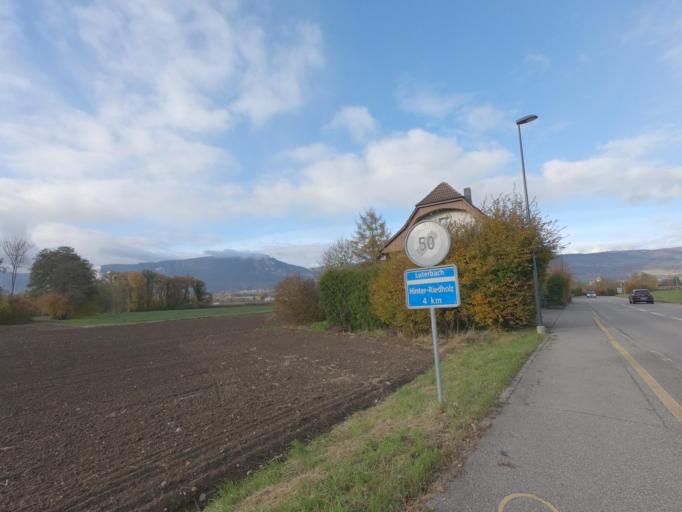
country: CH
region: Solothurn
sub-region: Bezirk Wasseramt
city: Luterbach
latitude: 47.2066
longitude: 7.5843
